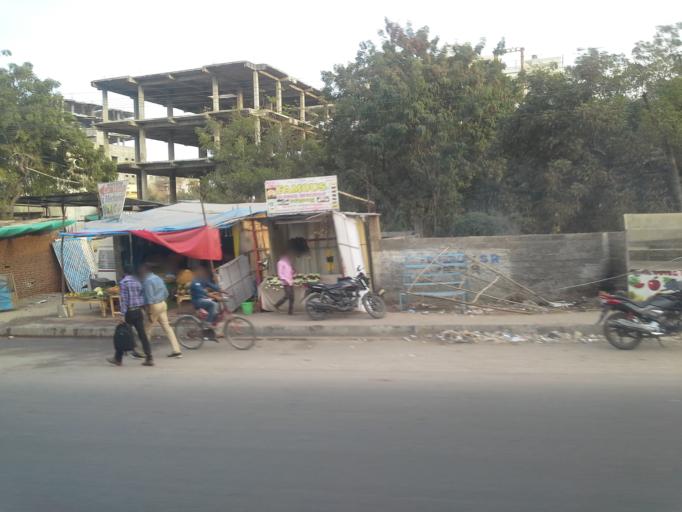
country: IN
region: Telangana
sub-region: Hyderabad
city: Hyderabad
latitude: 17.3644
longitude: 78.3953
